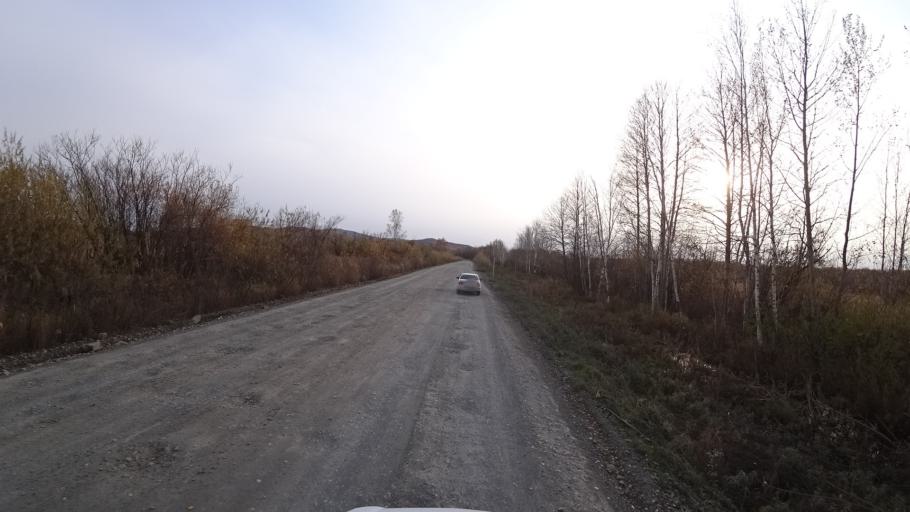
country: RU
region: Khabarovsk Krai
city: Amursk
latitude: 50.0706
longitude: 136.4873
